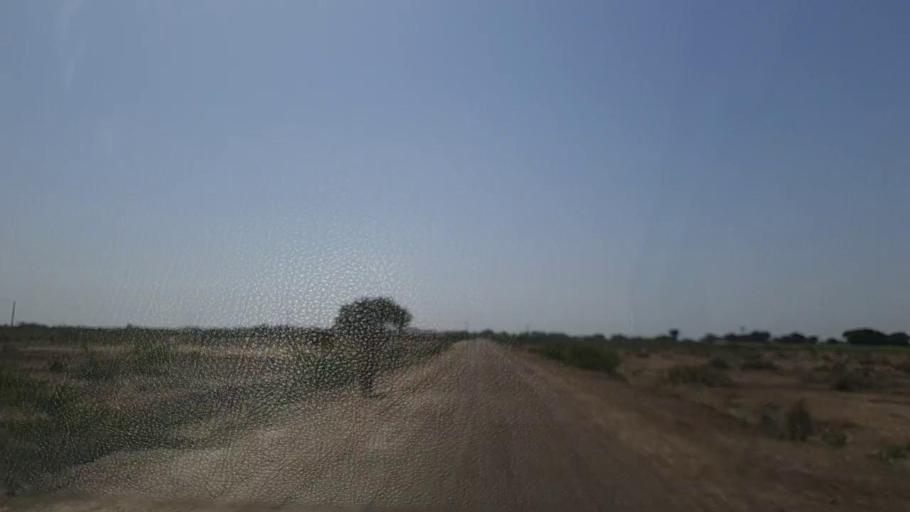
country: PK
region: Sindh
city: Samaro
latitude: 25.2369
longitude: 69.4543
